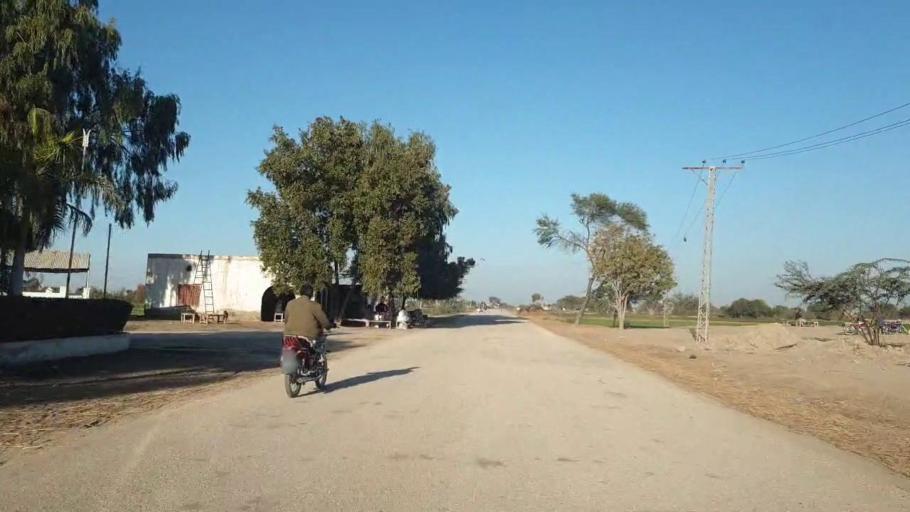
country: PK
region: Sindh
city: Dokri
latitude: 27.3689
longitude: 68.1170
